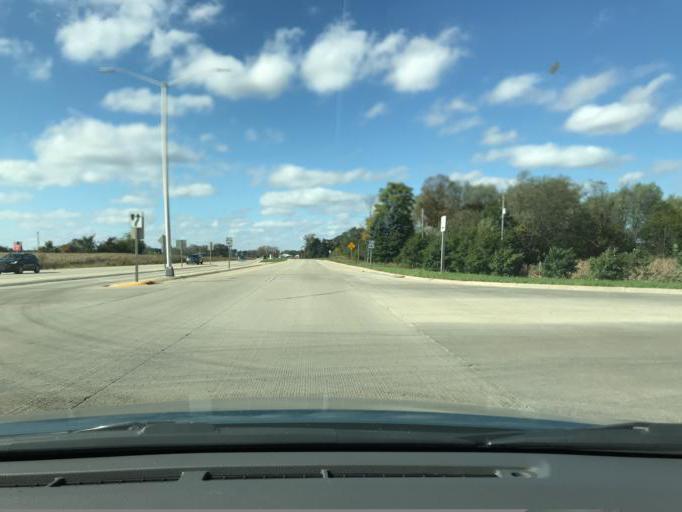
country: US
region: Wisconsin
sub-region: Kenosha County
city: Somers
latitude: 42.6160
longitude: -87.9548
